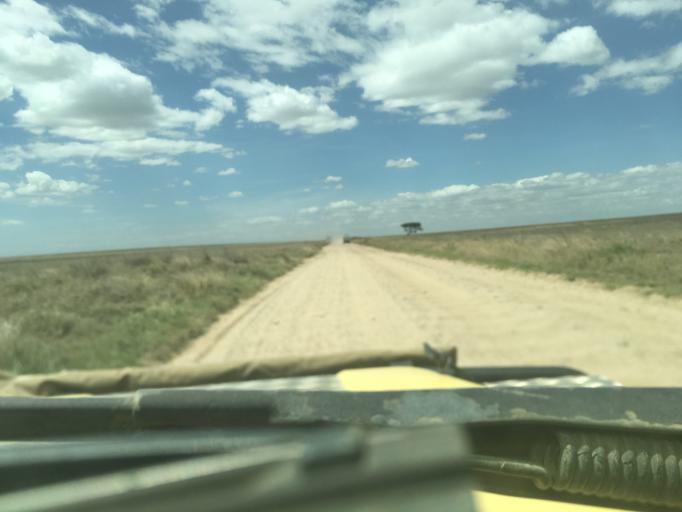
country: TZ
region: Mara
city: Mugumu
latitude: -2.5887
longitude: 34.8798
